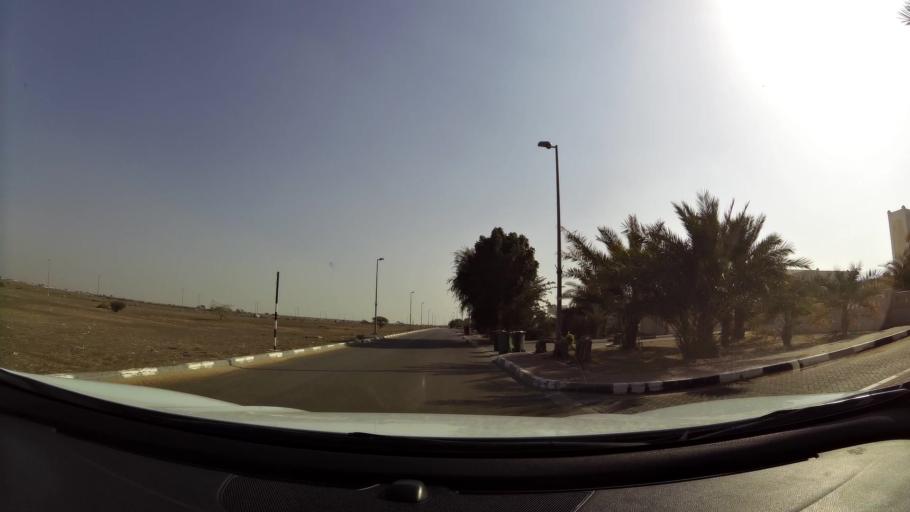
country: AE
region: Abu Dhabi
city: Al Ain
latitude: 24.0733
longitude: 55.8731
